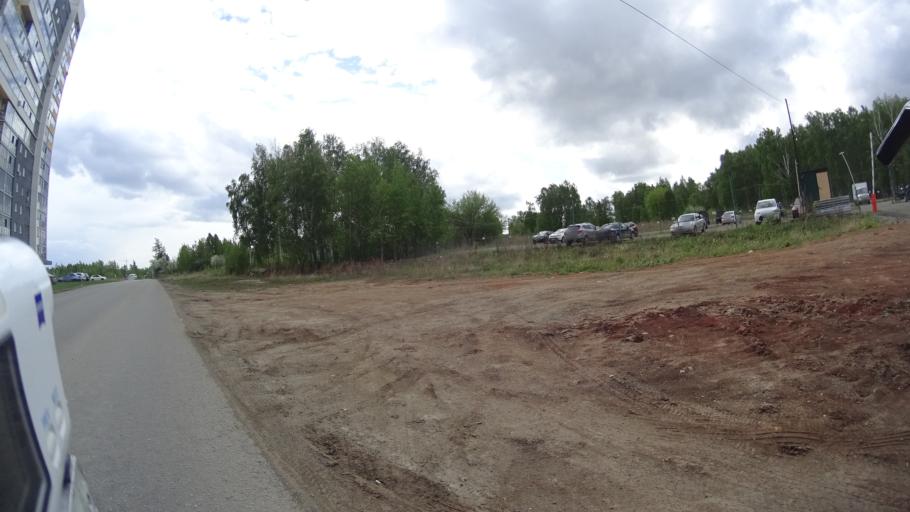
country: RU
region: Chelyabinsk
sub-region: Gorod Chelyabinsk
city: Chelyabinsk
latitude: 55.1608
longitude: 61.2856
